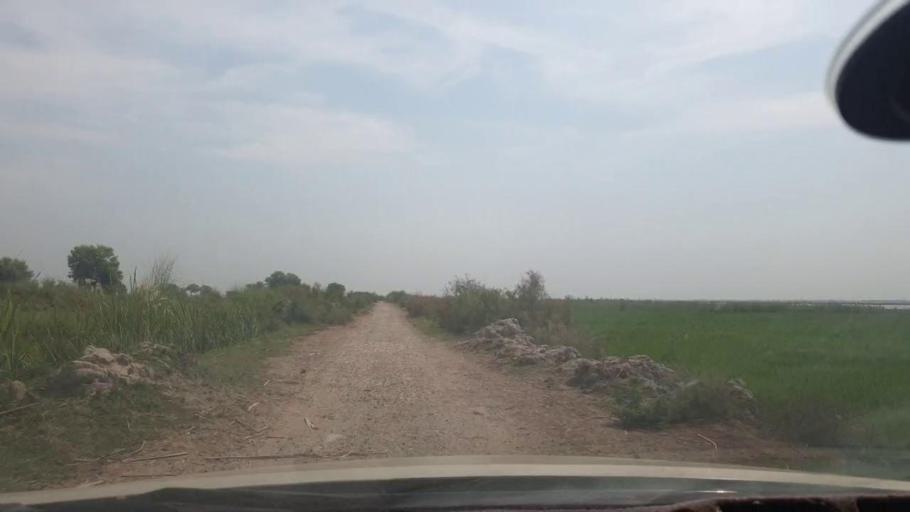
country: PK
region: Sindh
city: Jacobabad
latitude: 28.3177
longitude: 68.4884
